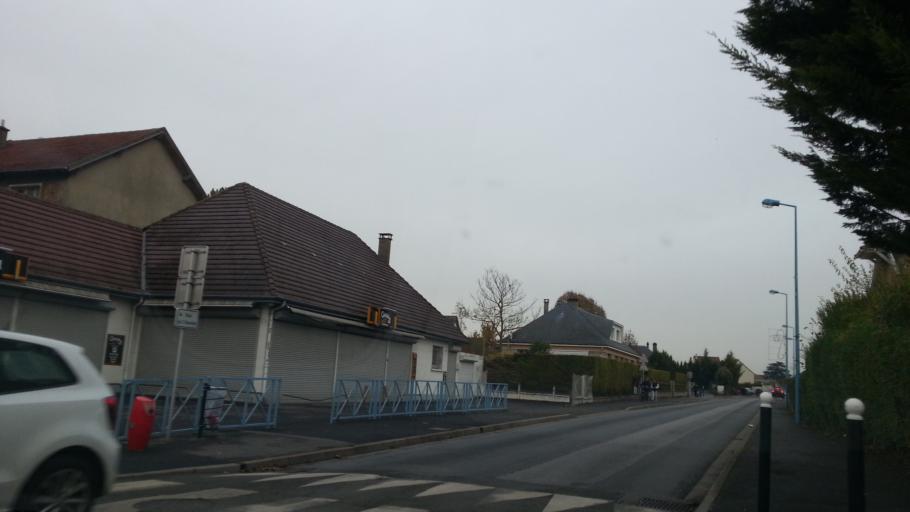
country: FR
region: Picardie
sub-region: Departement de l'Oise
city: Chambly
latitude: 49.1670
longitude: 2.2488
